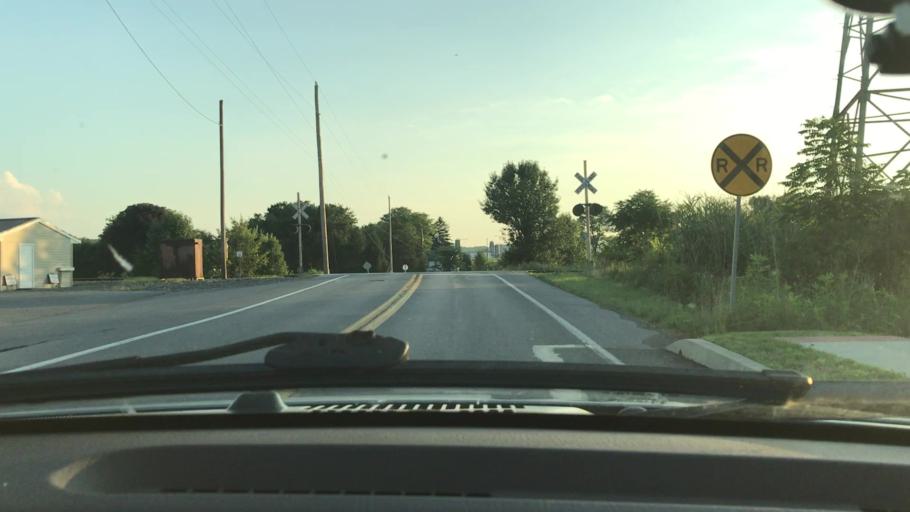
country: US
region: Pennsylvania
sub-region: Lancaster County
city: East Petersburg
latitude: 40.0973
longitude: -76.3609
